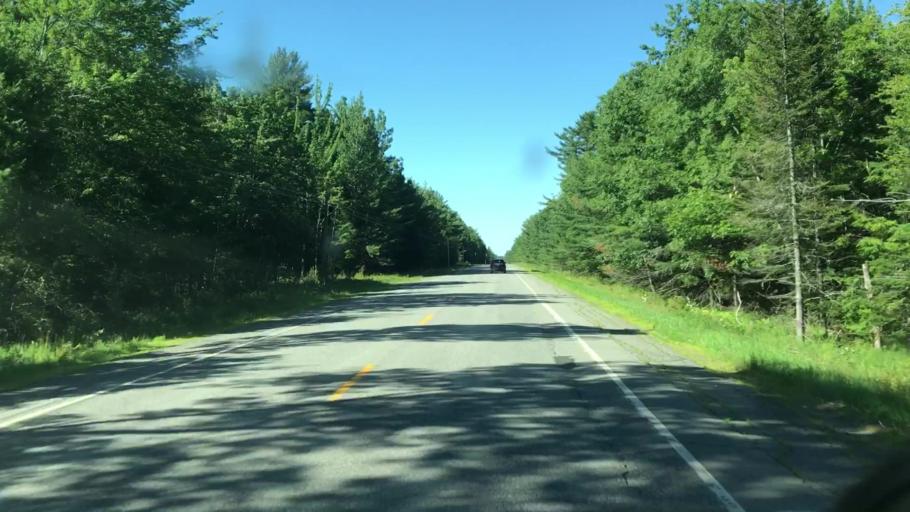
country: US
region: Maine
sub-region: Penobscot County
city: Enfield
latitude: 45.3158
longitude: -68.6033
